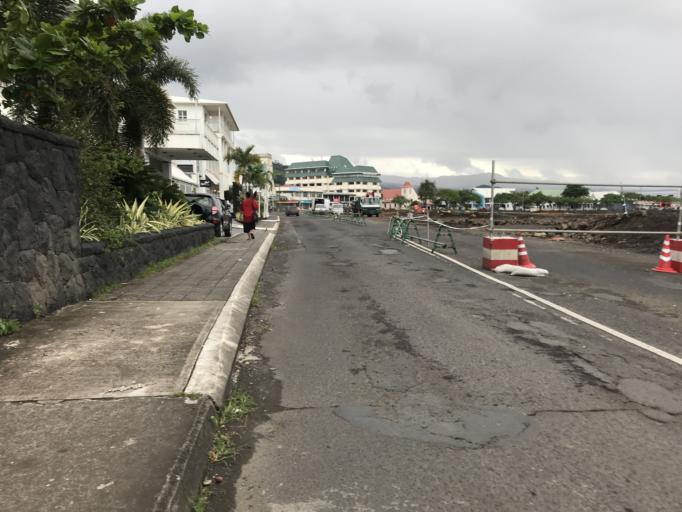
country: WS
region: Tuamasaga
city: Apia
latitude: -13.8319
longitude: -171.7604
